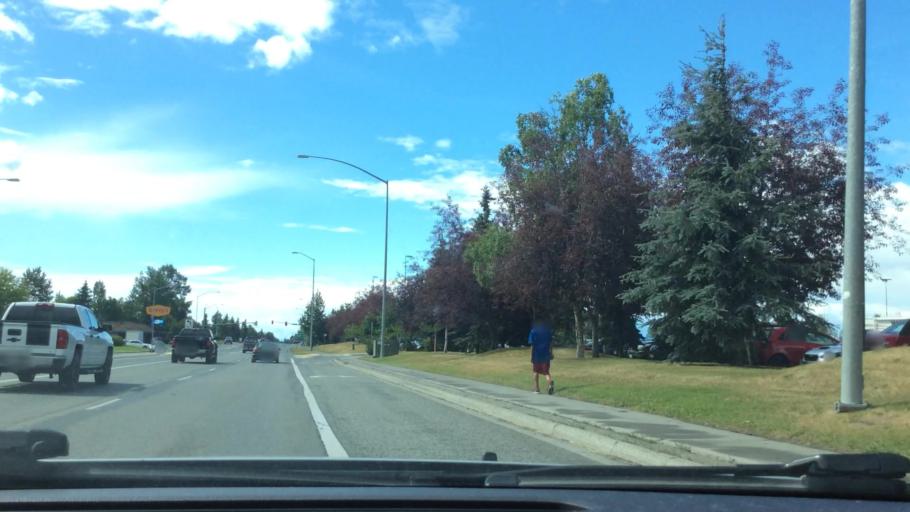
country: US
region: Alaska
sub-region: Anchorage Municipality
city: Anchorage
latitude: 61.2097
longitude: -149.8027
